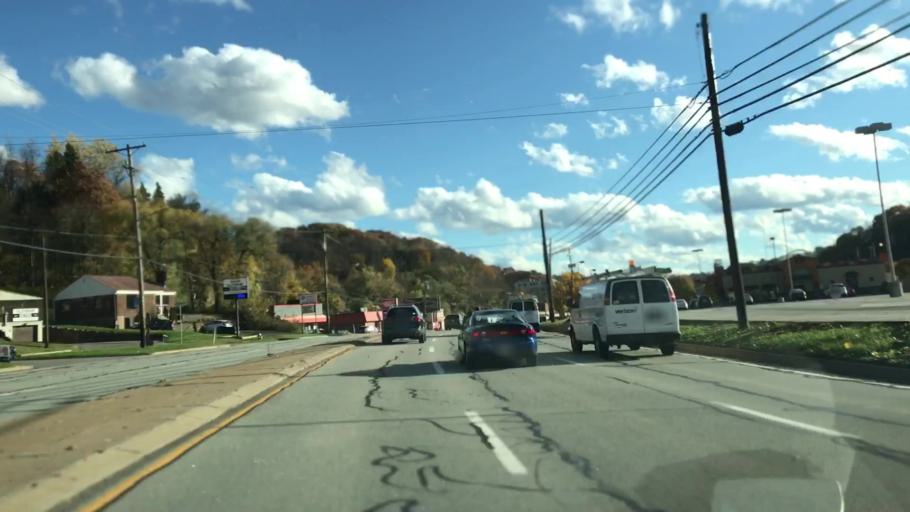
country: US
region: Pennsylvania
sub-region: Allegheny County
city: West View
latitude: 40.5272
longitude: -80.0061
